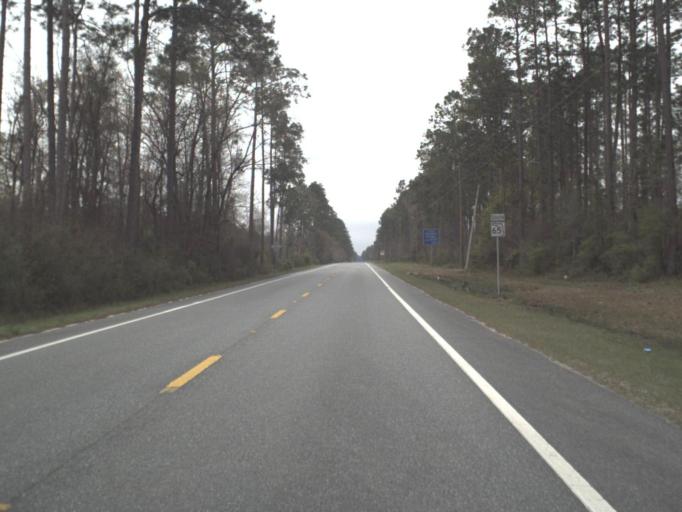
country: US
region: Florida
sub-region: Gulf County
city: Wewahitchka
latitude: 30.0132
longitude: -84.9789
